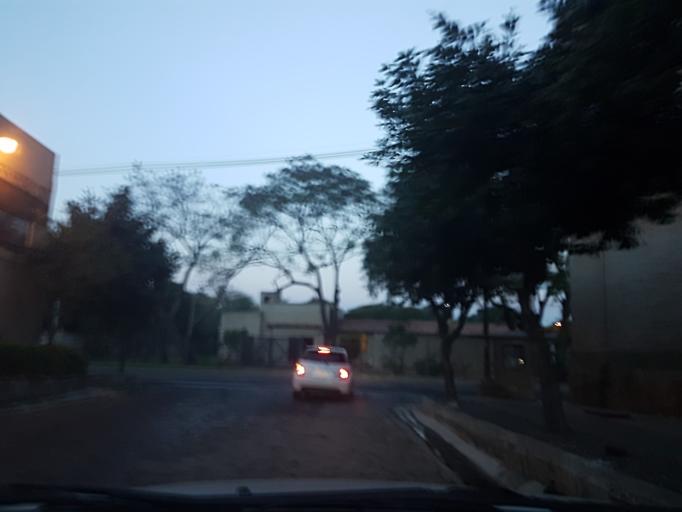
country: PY
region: Central
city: Colonia Mariano Roque Alonso
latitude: -25.2279
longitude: -57.5265
